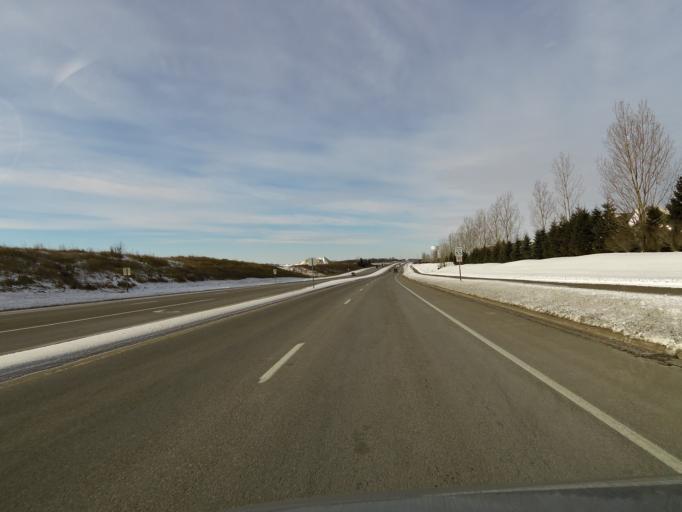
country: US
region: Minnesota
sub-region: Dakota County
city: Rosemount
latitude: 44.7172
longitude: -93.1574
